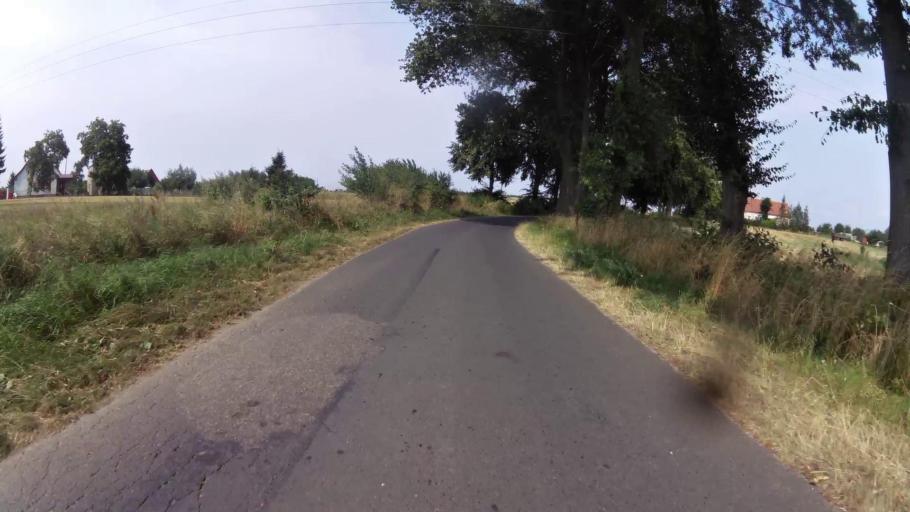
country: PL
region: West Pomeranian Voivodeship
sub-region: Powiat pyrzycki
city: Lipiany
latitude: 52.9750
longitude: 15.0229
